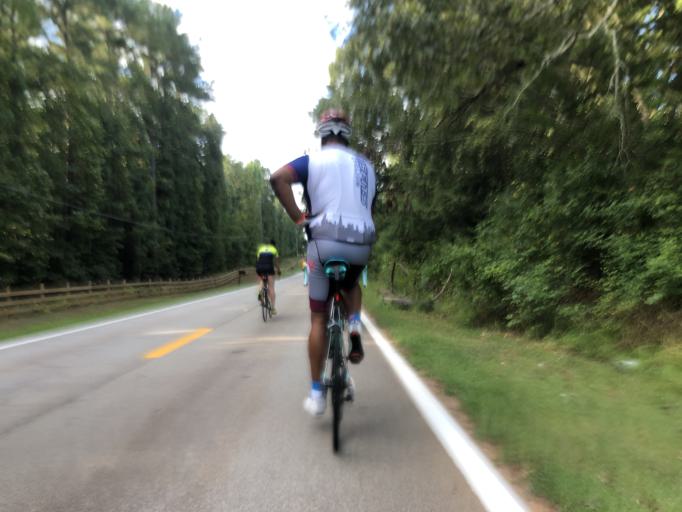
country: US
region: Georgia
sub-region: Fulton County
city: Palmetto
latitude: 33.5762
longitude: -84.6494
